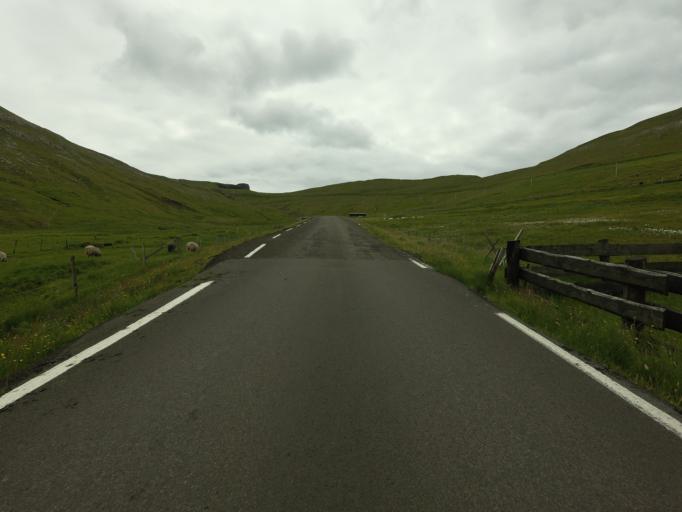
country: FO
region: Suduroy
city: Vagur
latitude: 61.4404
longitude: -6.7715
